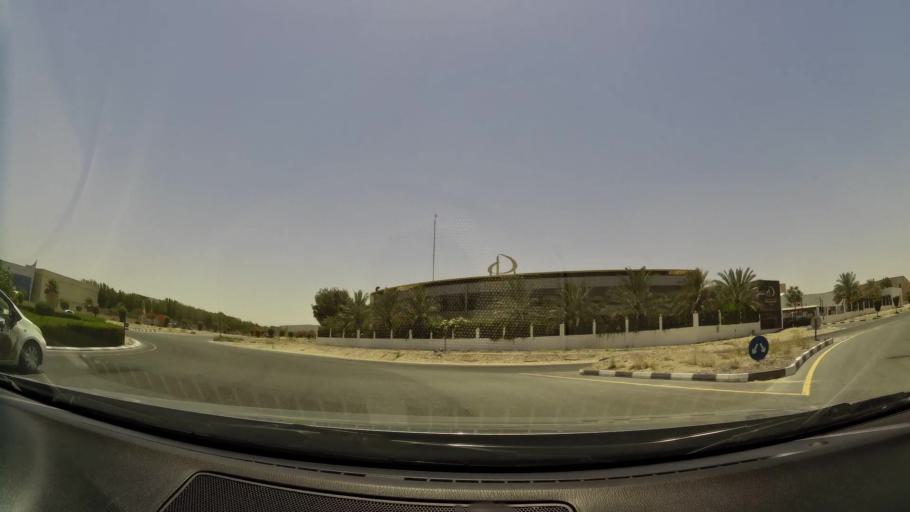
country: AE
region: Dubai
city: Dubai
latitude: 24.9846
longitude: 55.2069
